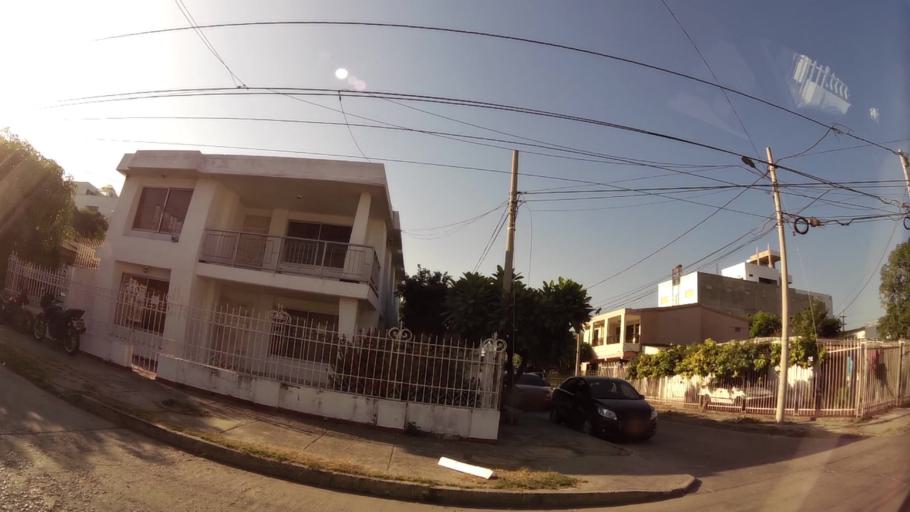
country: CO
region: Bolivar
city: Cartagena
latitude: 10.3981
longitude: -75.5210
